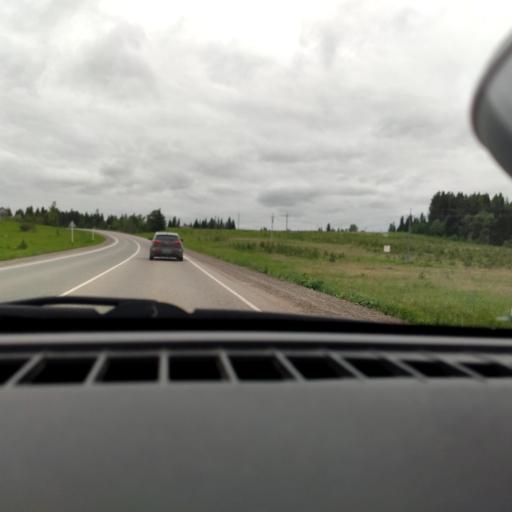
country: RU
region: Perm
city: Kultayevo
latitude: 57.8897
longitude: 55.7993
